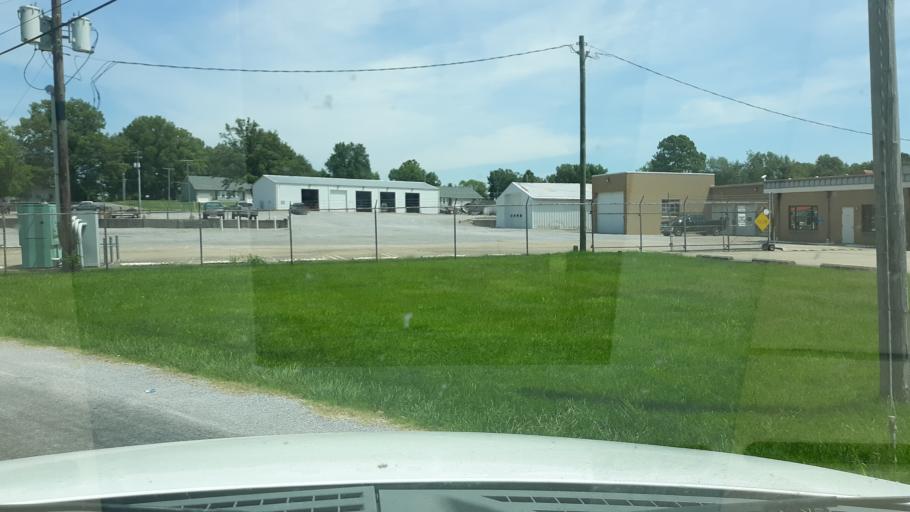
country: US
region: Illinois
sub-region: Saline County
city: Eldorado
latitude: 37.8034
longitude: -88.4320
